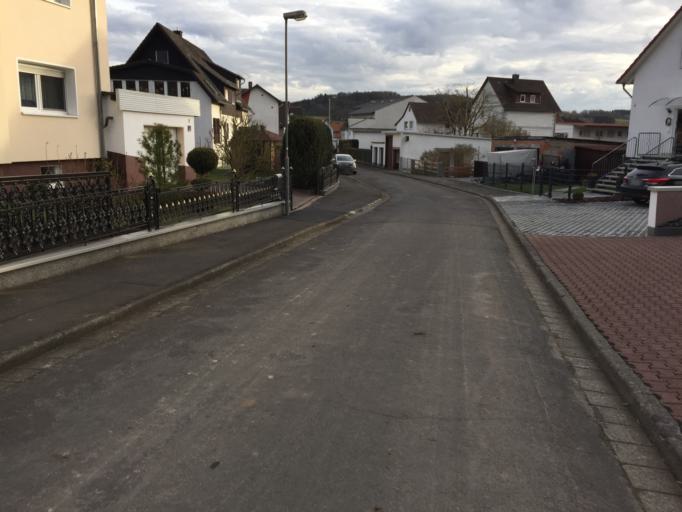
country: DE
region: Hesse
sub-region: Regierungsbezirk Giessen
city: Rabenau
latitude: 50.6789
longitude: 8.8593
